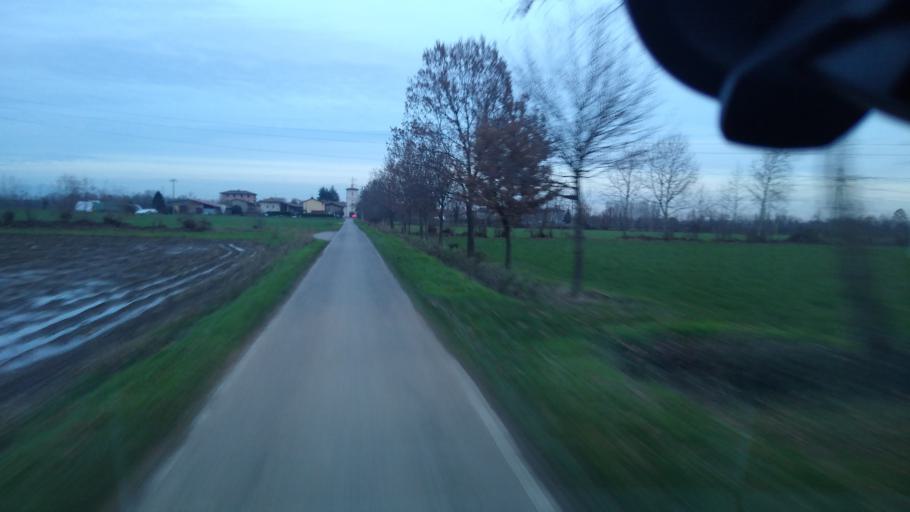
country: IT
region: Lombardy
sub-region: Provincia di Bergamo
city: Geromina
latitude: 45.5503
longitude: 9.5712
